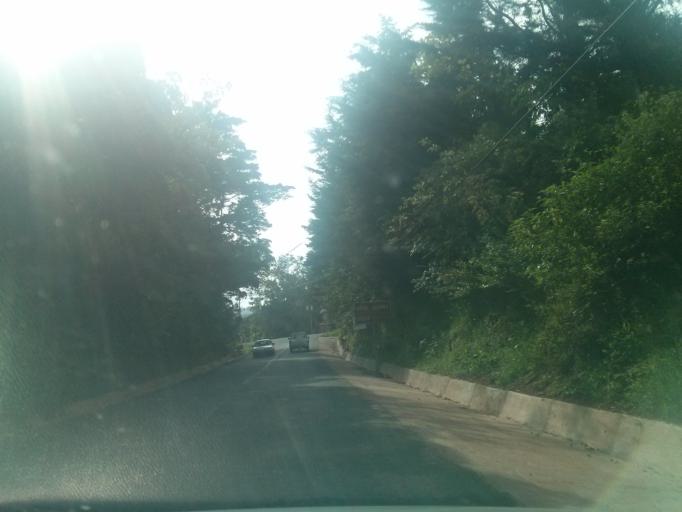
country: CR
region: Alajuela
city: Sabanilla
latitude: 10.1402
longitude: -84.1941
